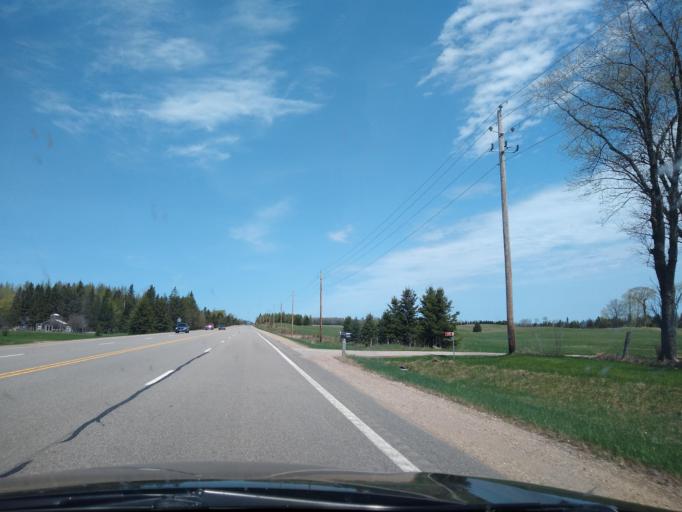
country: US
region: Michigan
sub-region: Delta County
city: Gladstone
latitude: 46.0866
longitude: -86.9807
